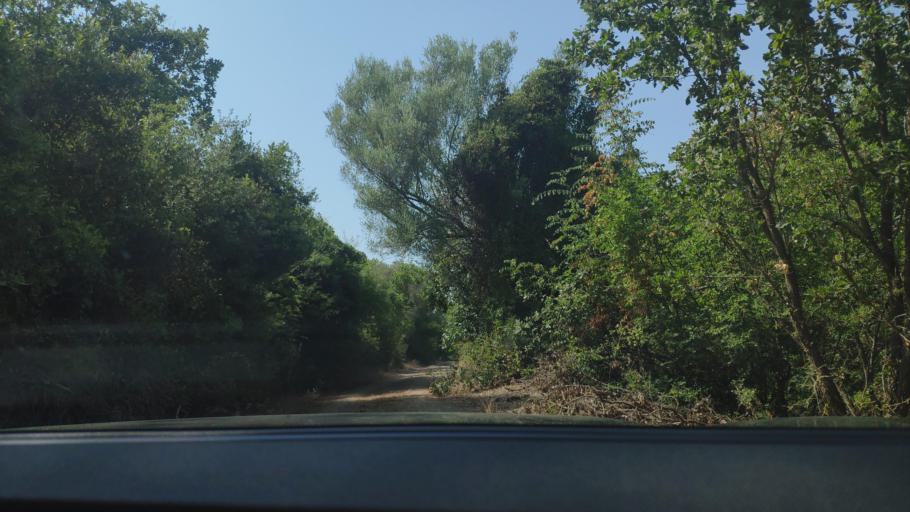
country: GR
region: West Greece
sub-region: Nomos Aitolias kai Akarnanias
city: Fitiai
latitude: 38.7302
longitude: 21.1845
